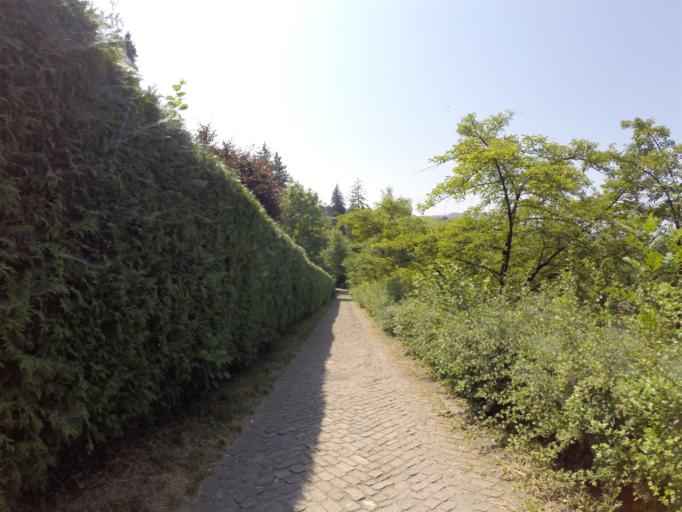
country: CH
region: Bern
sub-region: Bern-Mittelland District
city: Bern
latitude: 46.9494
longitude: 7.4606
